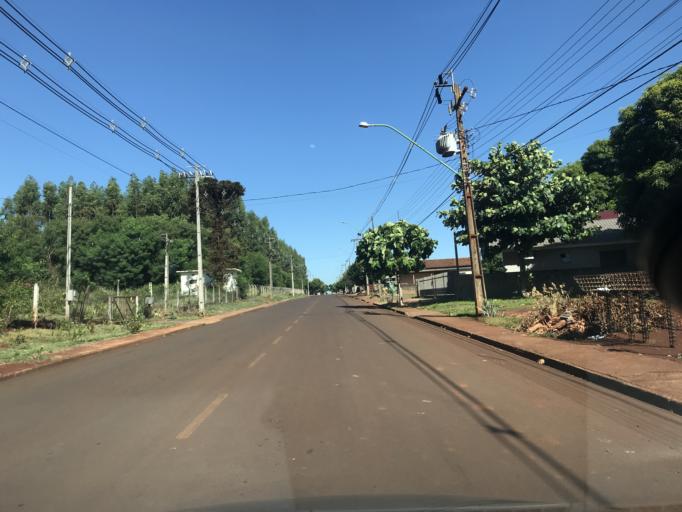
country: BR
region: Parana
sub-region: Palotina
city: Palotina
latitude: -24.2746
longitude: -53.8293
